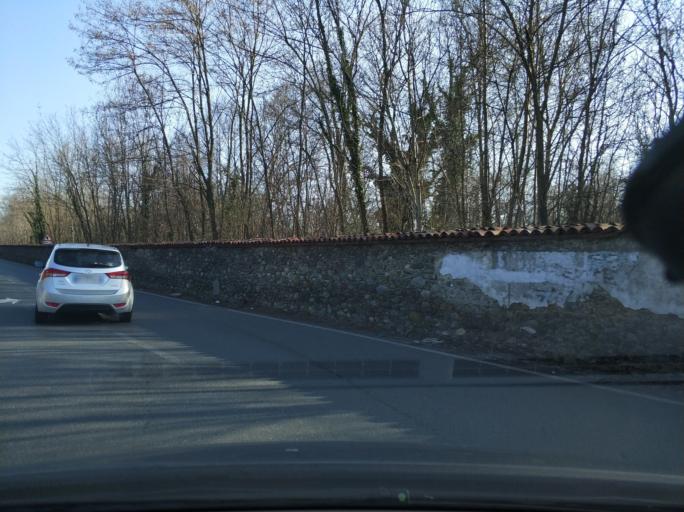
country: IT
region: Piedmont
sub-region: Provincia di Torino
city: Robassomero
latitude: 45.1946
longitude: 7.5621
